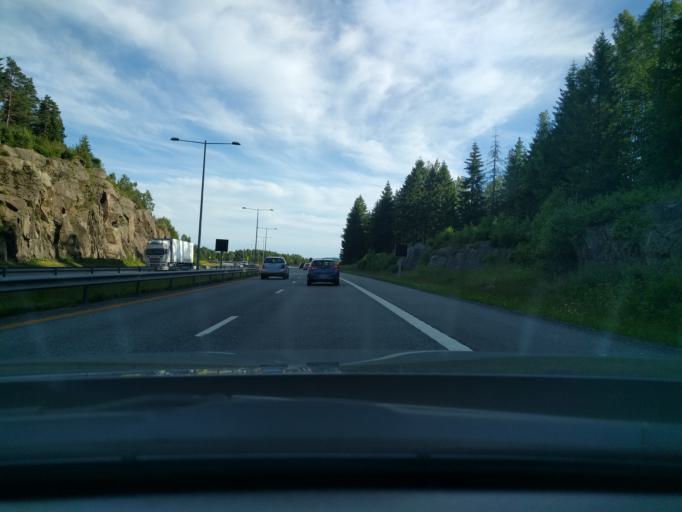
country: NO
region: Vestfold
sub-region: Sande
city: Sande
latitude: 59.5442
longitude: 10.1781
